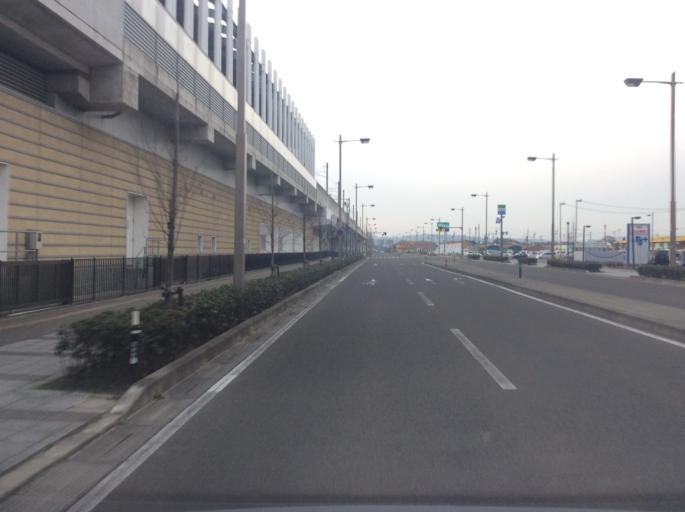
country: JP
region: Miyagi
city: Iwanuma
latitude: 38.1596
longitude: 140.9182
